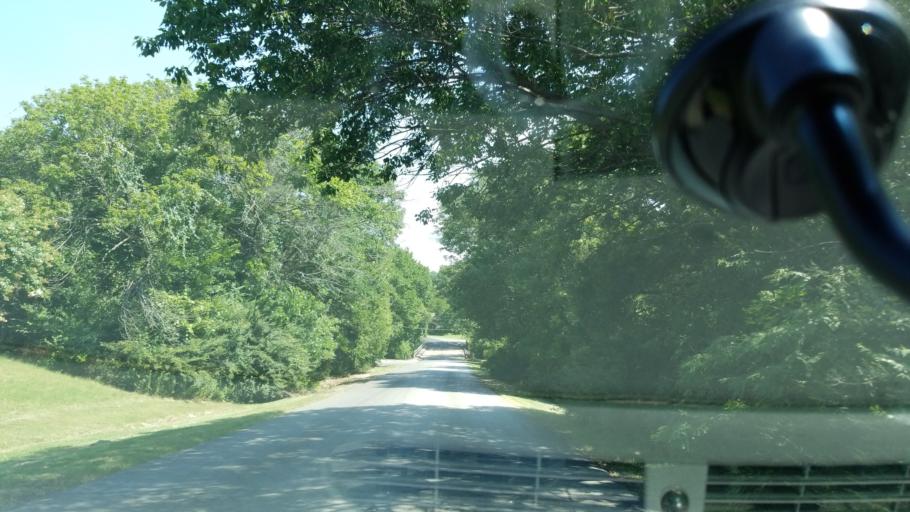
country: US
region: Texas
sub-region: Dallas County
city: Cockrell Hill
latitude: 32.7066
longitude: -96.8810
